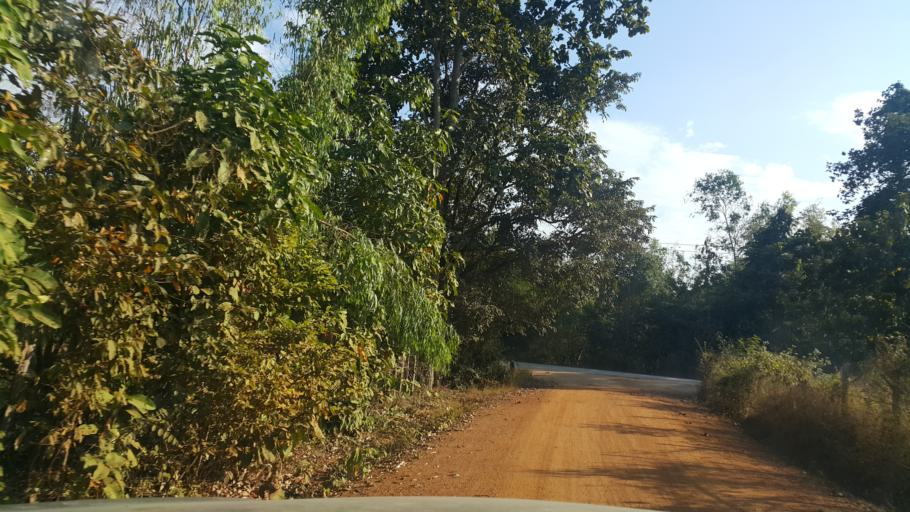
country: TH
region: Lampang
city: Hang Chat
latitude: 18.2601
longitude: 99.3676
